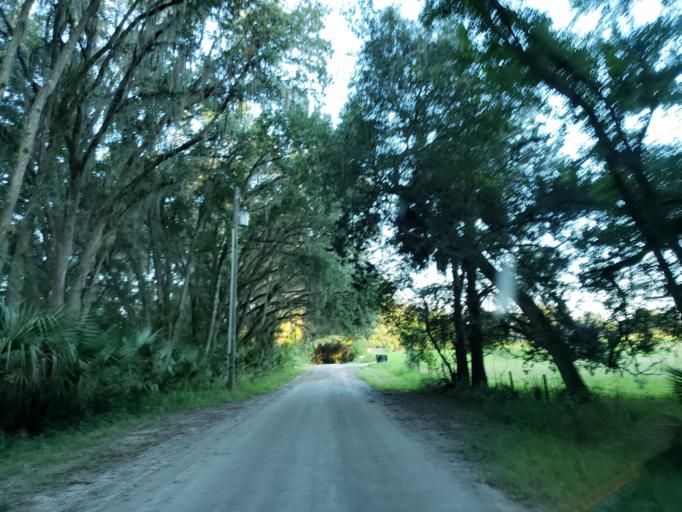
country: US
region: Florida
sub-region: Alachua County
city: Gainesville
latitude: 29.4919
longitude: -82.2808
